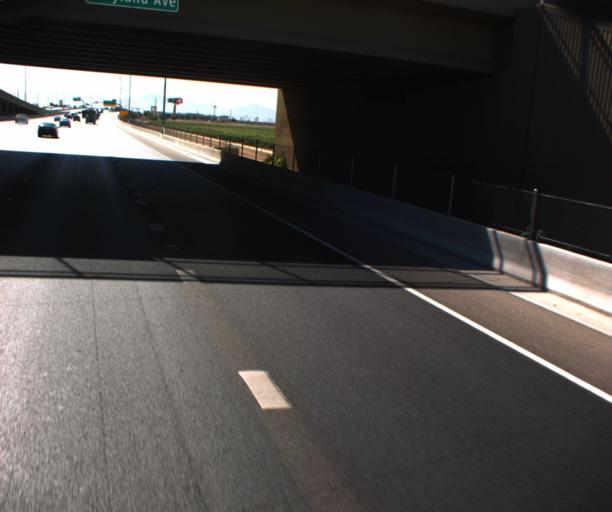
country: US
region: Arizona
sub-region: Maricopa County
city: Peoria
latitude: 33.5303
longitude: -112.2695
